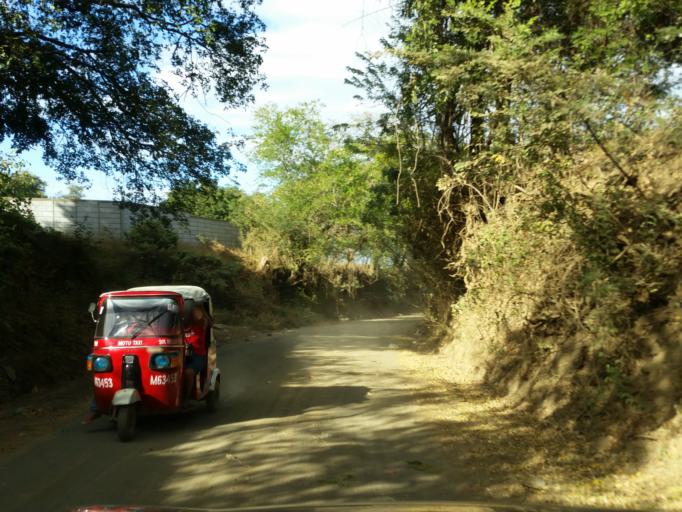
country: NI
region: Managua
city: Managua
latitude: 12.0941
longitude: -86.2625
